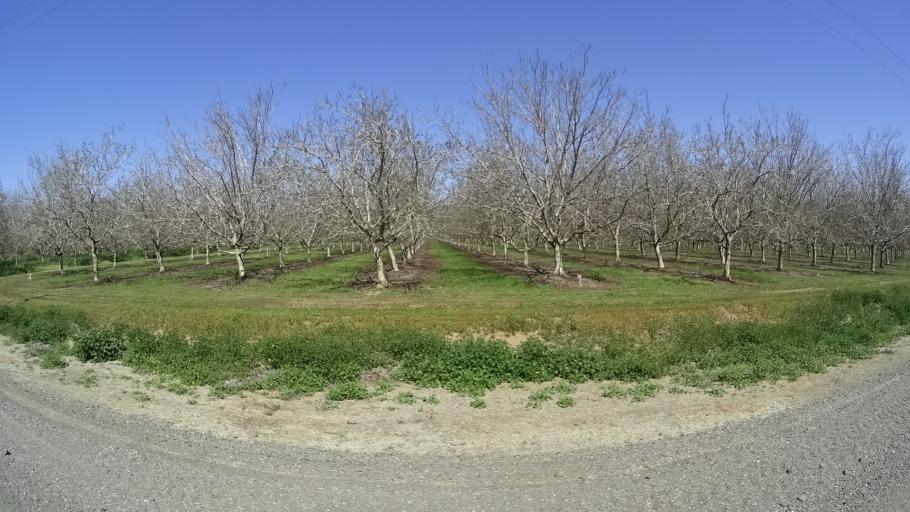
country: US
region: California
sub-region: Glenn County
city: Willows
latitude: 39.4644
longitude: -121.9787
